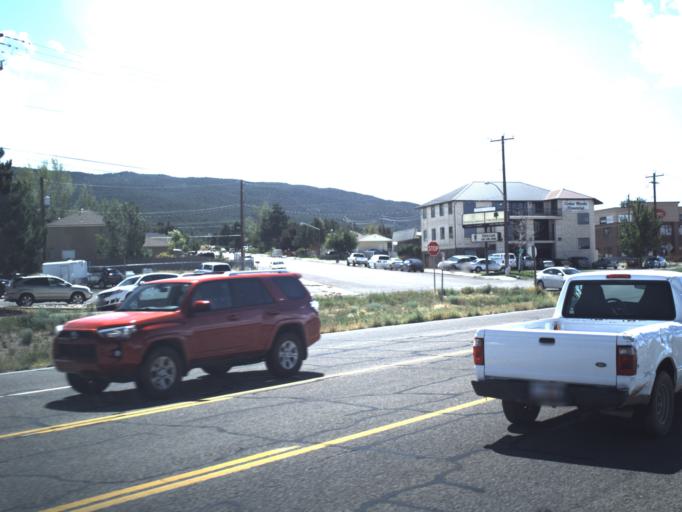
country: US
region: Utah
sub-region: Iron County
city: Cedar City
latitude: 37.6587
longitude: -113.0737
